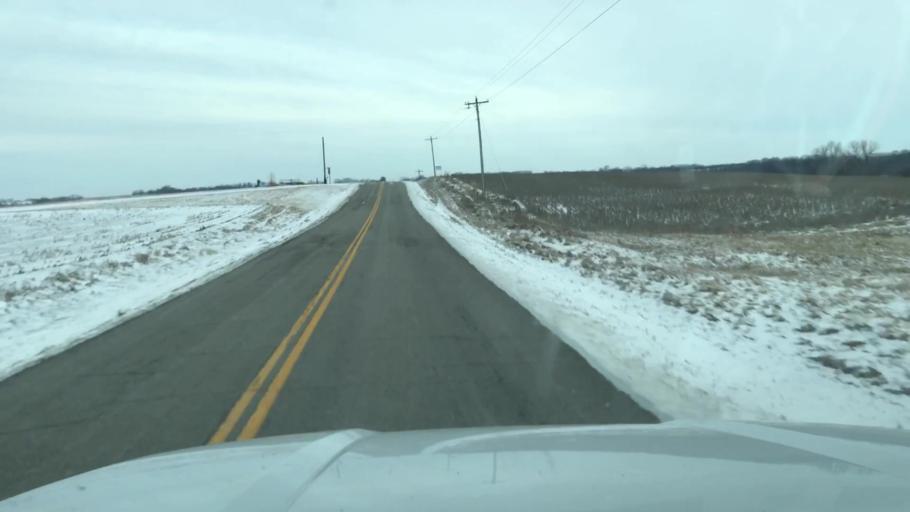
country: US
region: Missouri
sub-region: Holt County
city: Oregon
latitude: 40.1007
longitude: -94.9924
